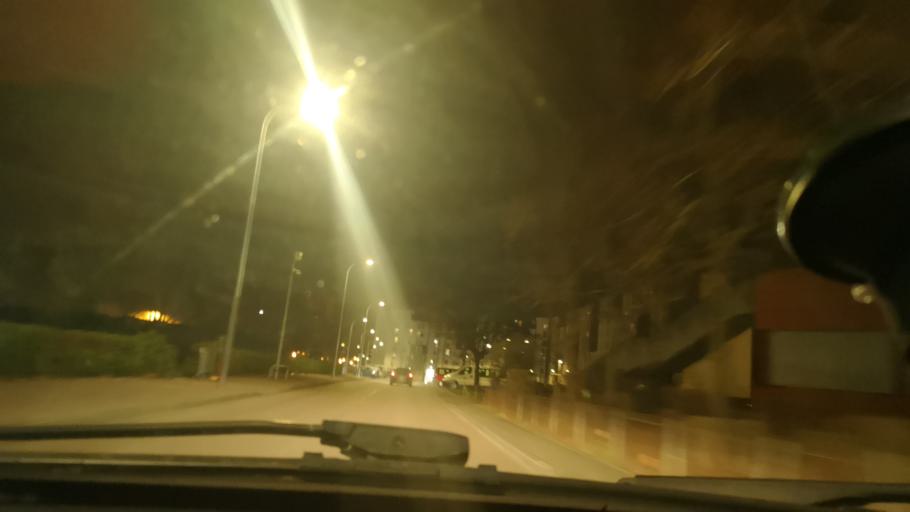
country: FR
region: Bourgogne
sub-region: Departement de Saone-et-Loire
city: Crissey
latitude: 46.7998
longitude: 4.8666
